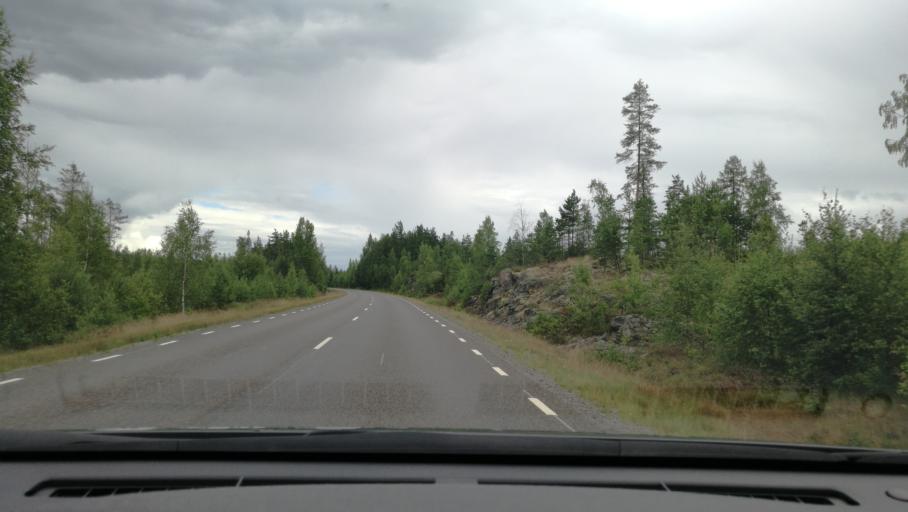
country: SE
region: OEstergoetland
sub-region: Norrkopings Kommun
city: Svartinge
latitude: 58.8030
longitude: 15.9428
